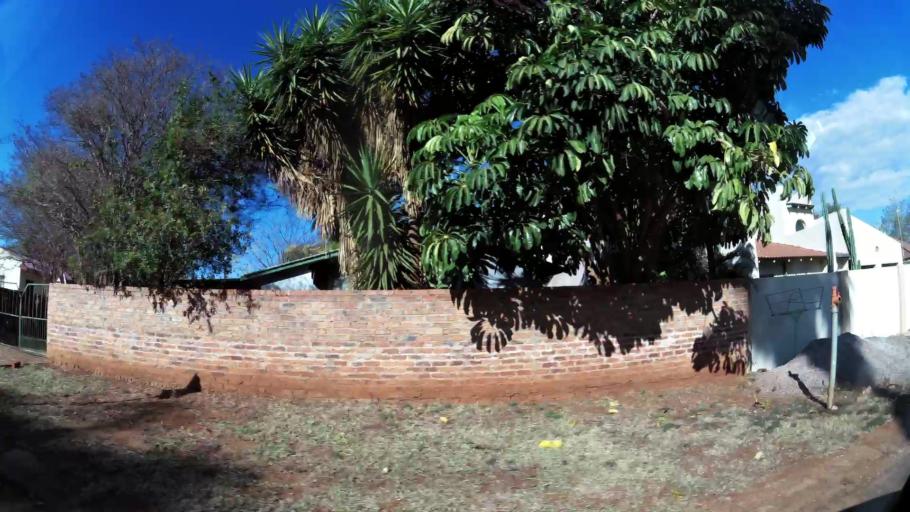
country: ZA
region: Limpopo
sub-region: Waterberg District Municipality
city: Mokopane
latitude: -24.1851
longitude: 28.9947
